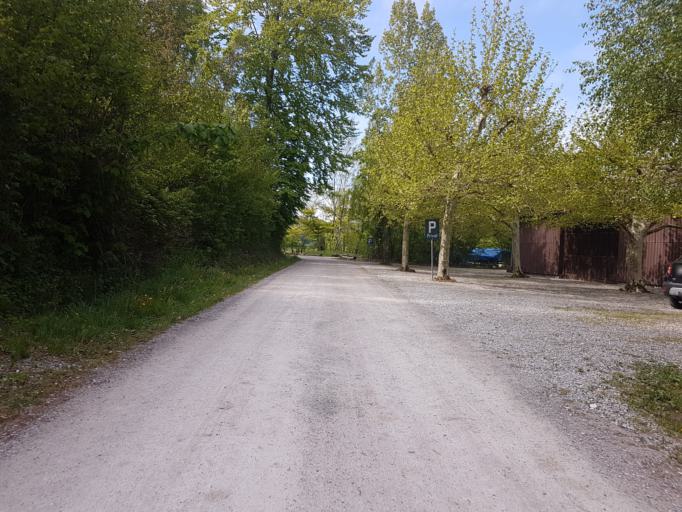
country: CH
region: Bern
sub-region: Seeland District
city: Tauffelen
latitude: 47.0707
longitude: 7.1921
